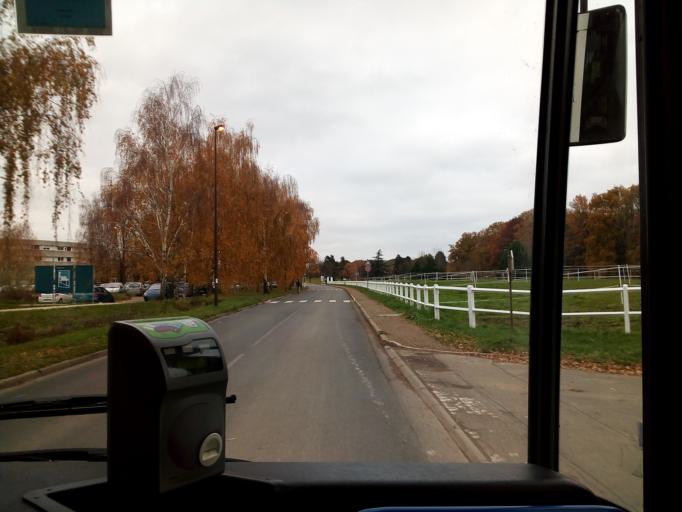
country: FR
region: Ile-de-France
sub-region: Departement de l'Essonne
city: Vauhallan
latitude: 48.7101
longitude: 2.2075
